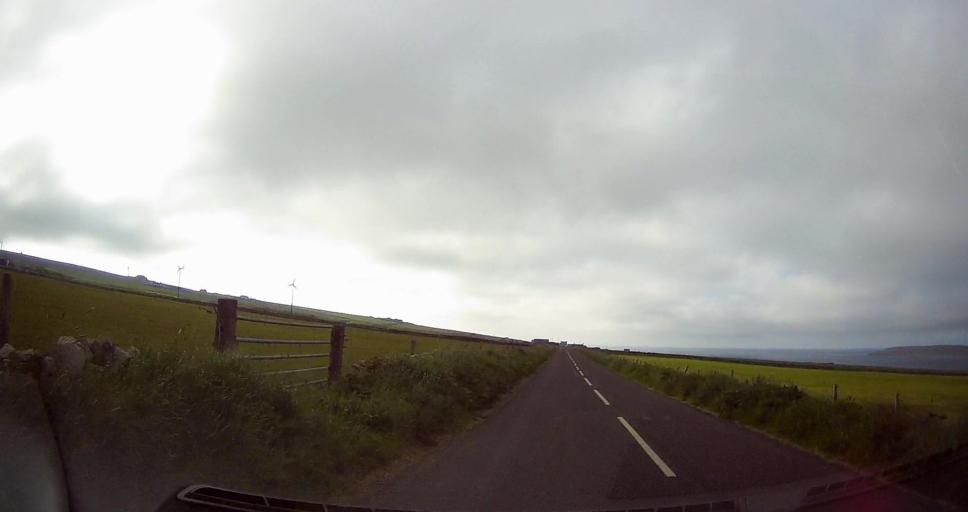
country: GB
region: Scotland
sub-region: Orkney Islands
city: Orkney
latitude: 59.1187
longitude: -3.1196
